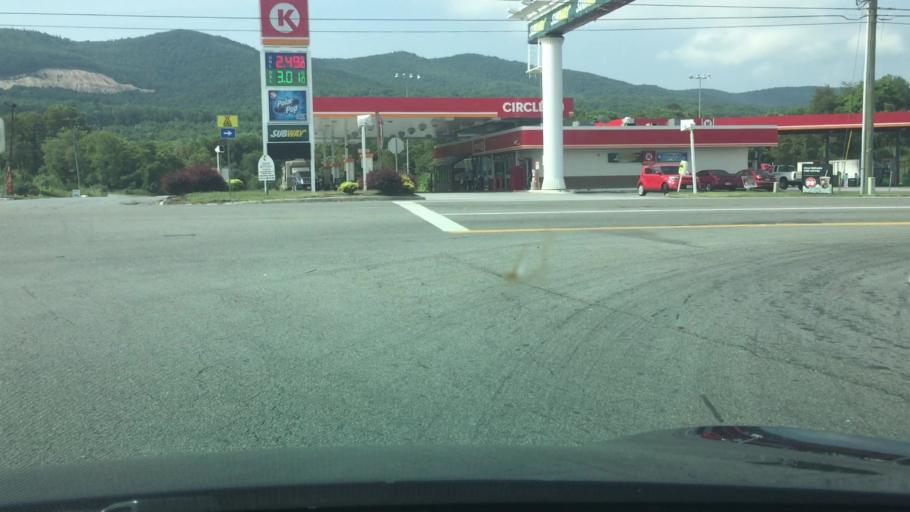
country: US
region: Virginia
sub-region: Wythe County
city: Wytheville
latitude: 36.9366
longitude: -80.9945
